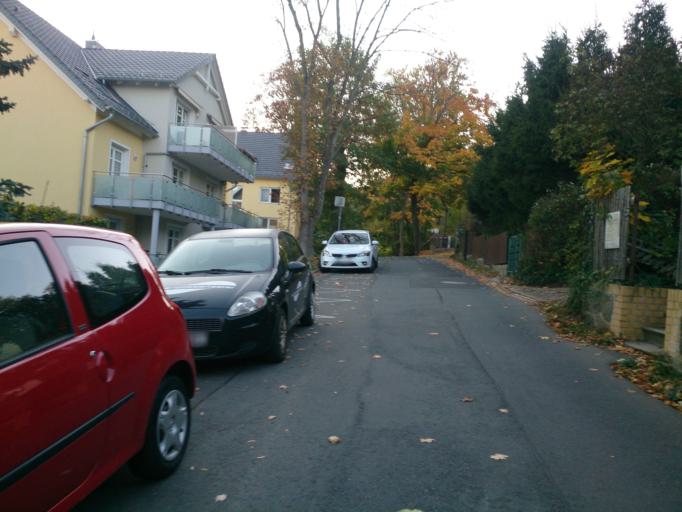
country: DE
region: Saxony-Anhalt
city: Wernigerode
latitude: 51.8287
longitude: 10.7777
